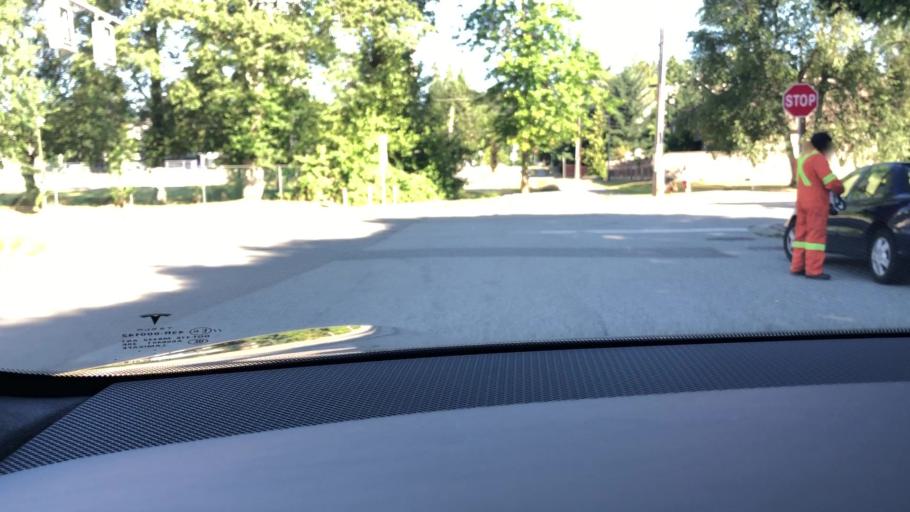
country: CA
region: British Columbia
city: New Westminster
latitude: 49.2113
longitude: -122.9521
